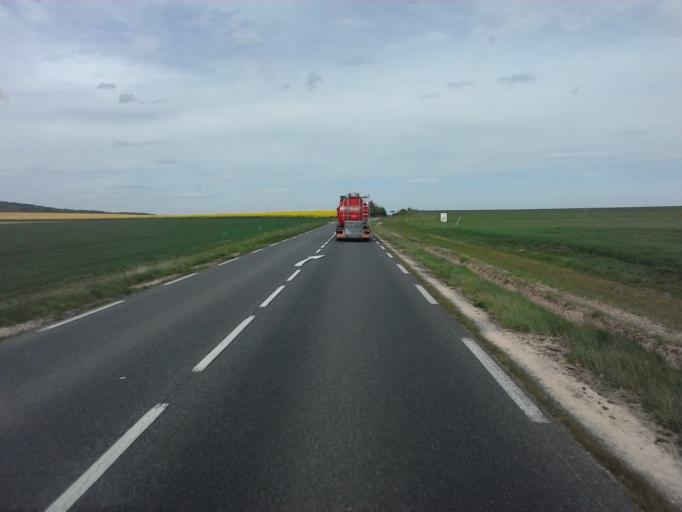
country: FR
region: Bourgogne
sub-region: Departement de l'Yonne
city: Neuvy-Sautour
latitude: 48.0697
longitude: 3.8148
